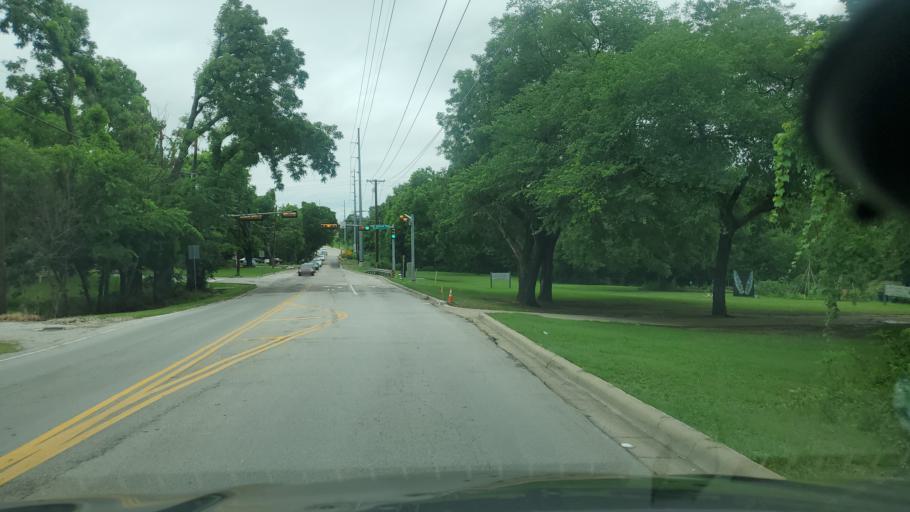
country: US
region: Texas
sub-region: Dallas County
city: Sachse
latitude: 32.9530
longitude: -96.6268
